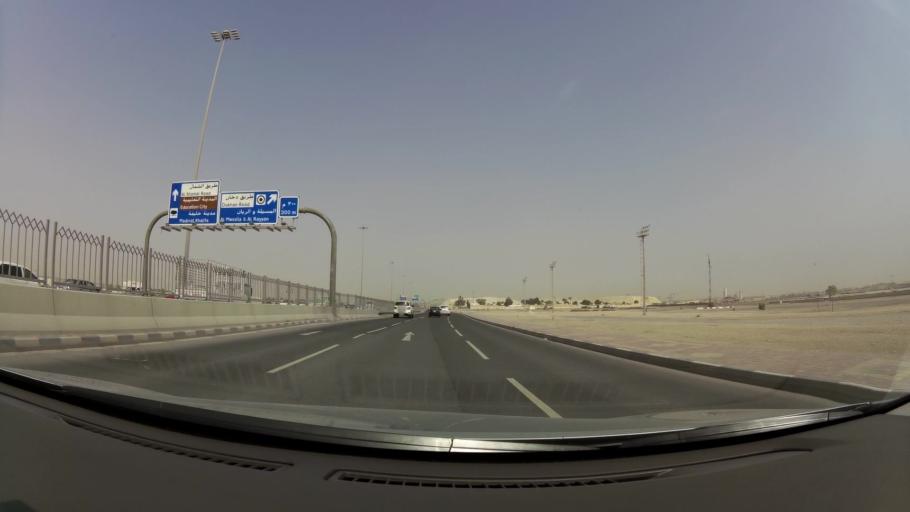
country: QA
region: Baladiyat ad Dawhah
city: Doha
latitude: 25.2812
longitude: 51.4856
